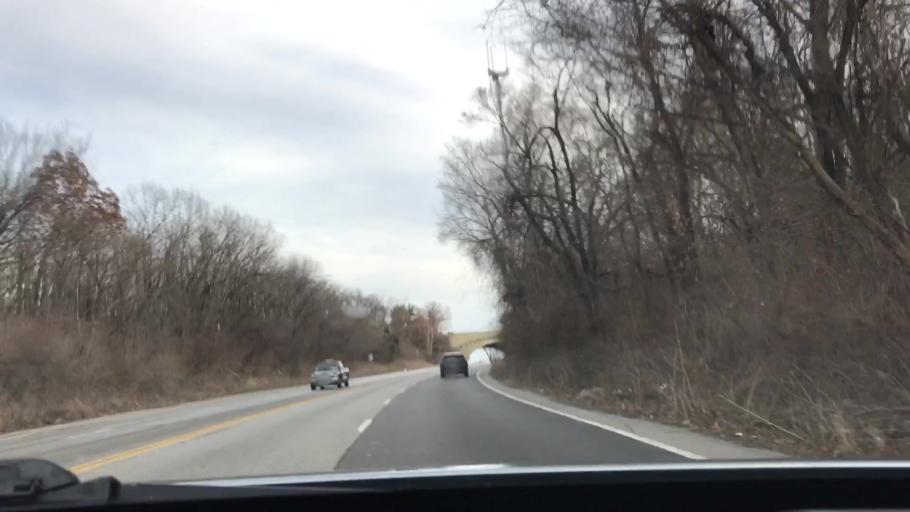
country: US
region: Missouri
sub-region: Jackson County
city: Sugar Creek
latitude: 39.0932
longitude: -94.4805
